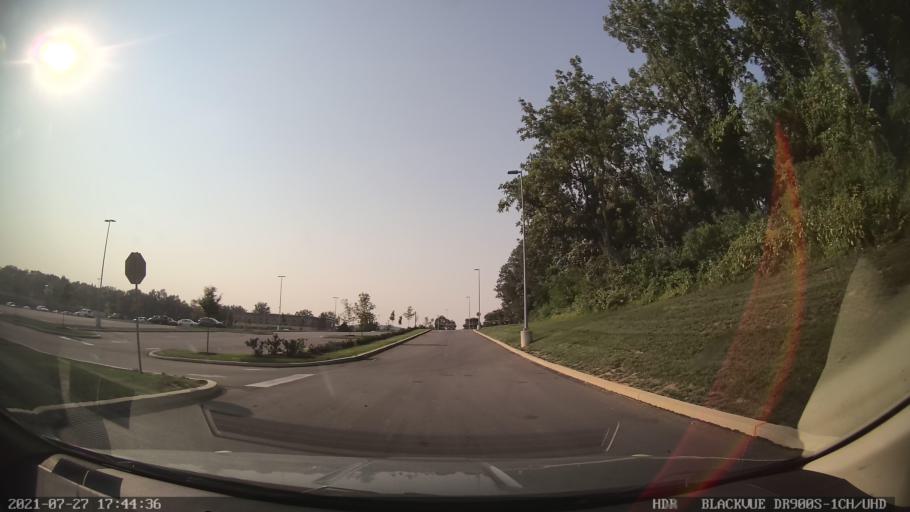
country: US
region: Pennsylvania
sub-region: Berks County
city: River View Park
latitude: 40.3727
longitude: -75.9709
